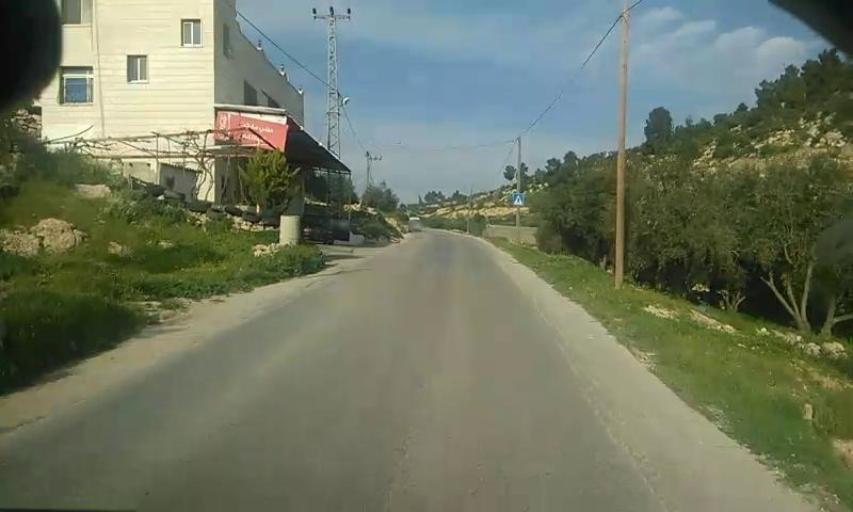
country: PS
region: West Bank
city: Tarqumya
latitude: 31.5836
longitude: 35.0219
